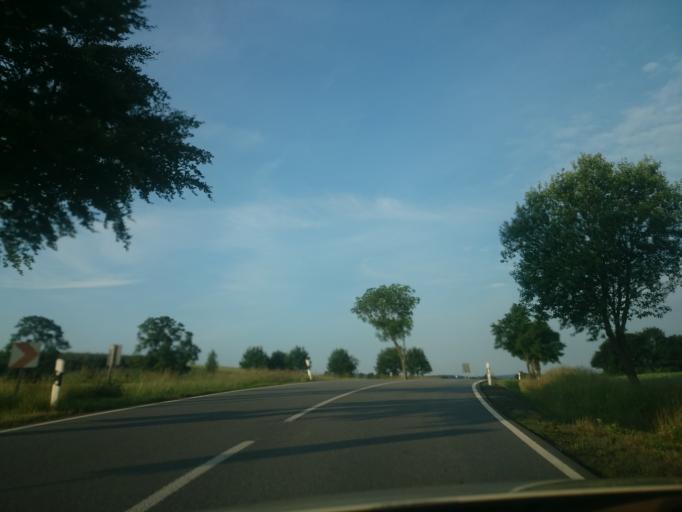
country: DE
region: Saxony
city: Pockau
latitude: 50.7183
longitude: 13.2568
